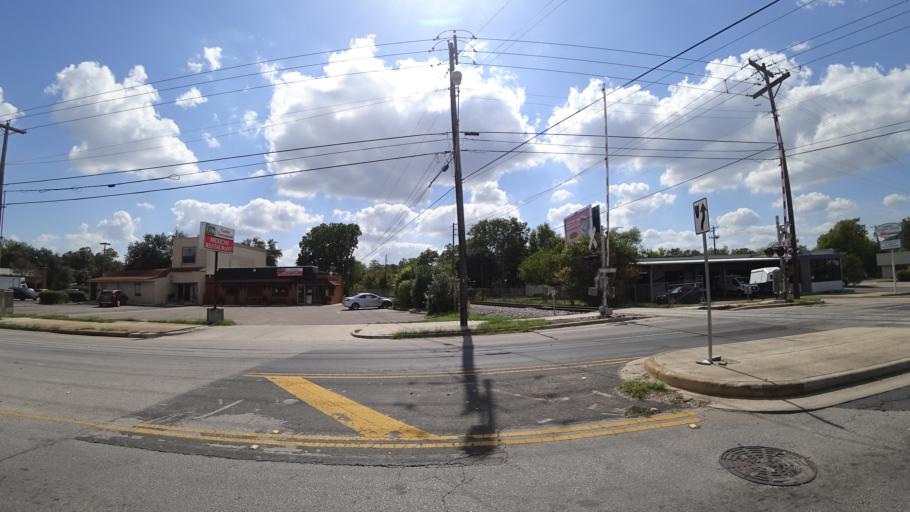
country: US
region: Texas
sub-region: Travis County
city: Austin
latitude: 30.3522
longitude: -97.7224
